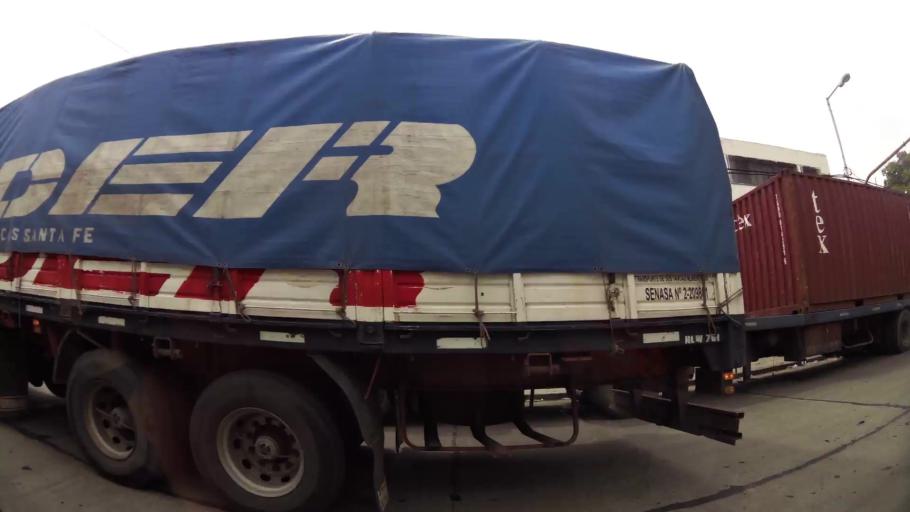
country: AR
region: Buenos Aires
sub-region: Partido de Avellaneda
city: Avellaneda
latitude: -34.6499
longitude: -58.3435
